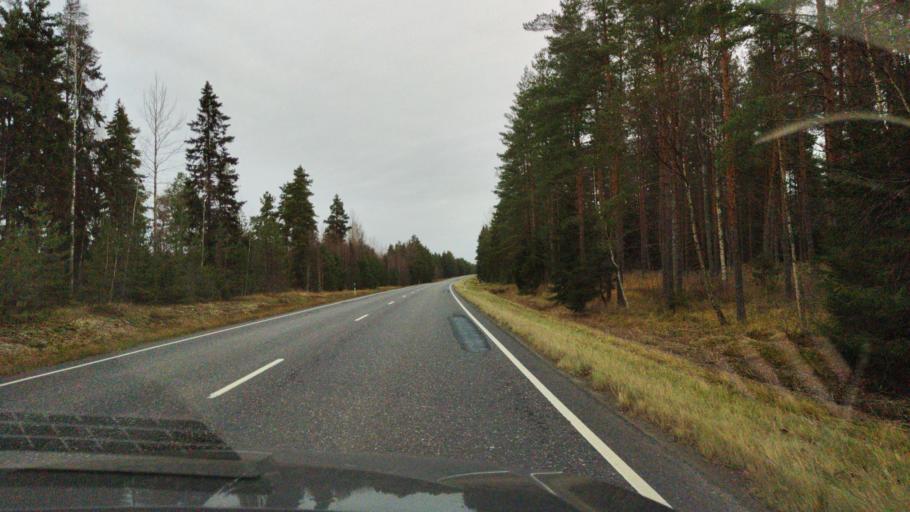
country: FI
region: Varsinais-Suomi
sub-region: Loimaa
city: Ylaene
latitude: 60.9037
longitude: 22.4079
